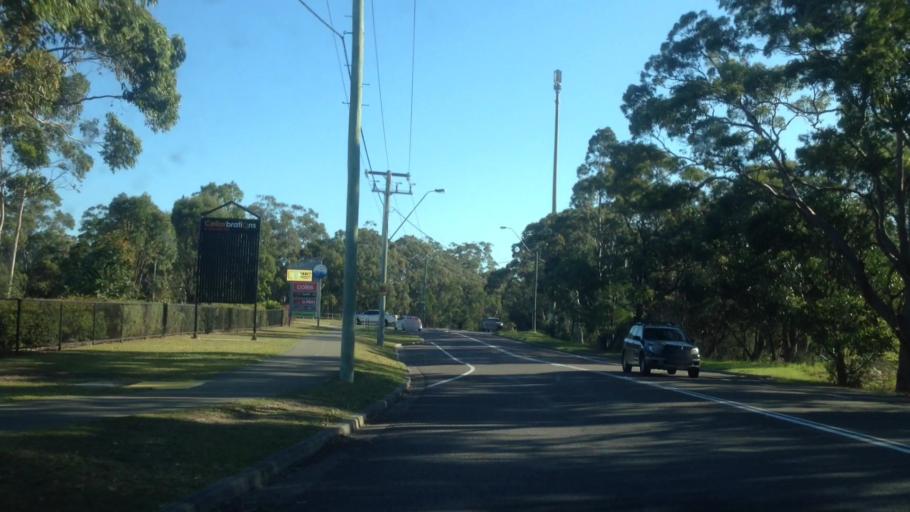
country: AU
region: New South Wales
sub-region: Lake Macquarie Shire
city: Dora Creek
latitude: -33.1105
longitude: 151.5314
